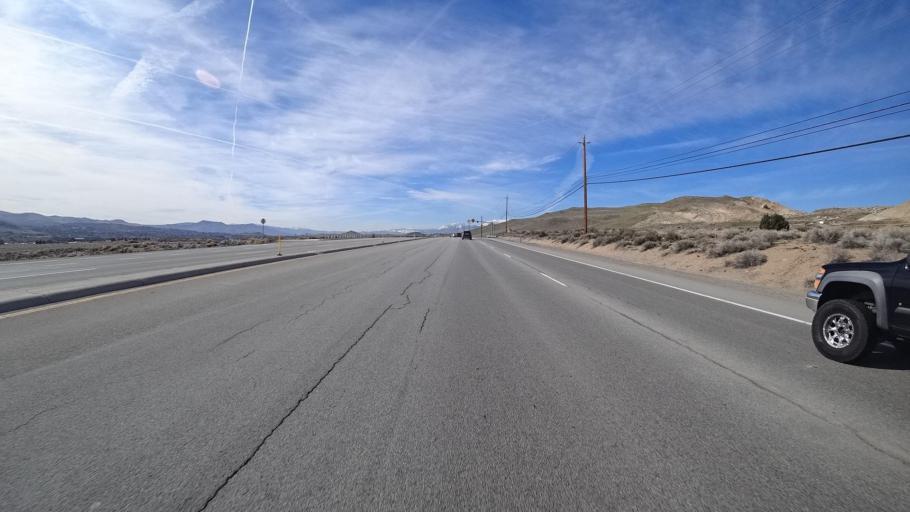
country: US
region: Nevada
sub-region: Washoe County
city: Spanish Springs
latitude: 39.6115
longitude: -119.7301
